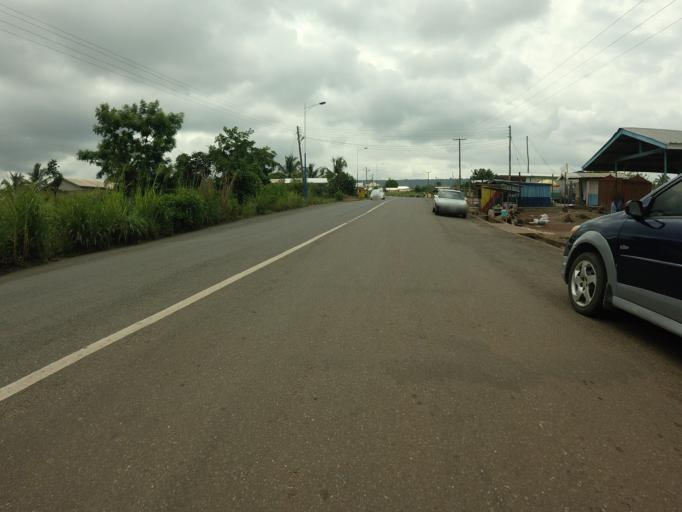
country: GH
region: Volta
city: Ho
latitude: 6.6210
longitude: 0.4955
